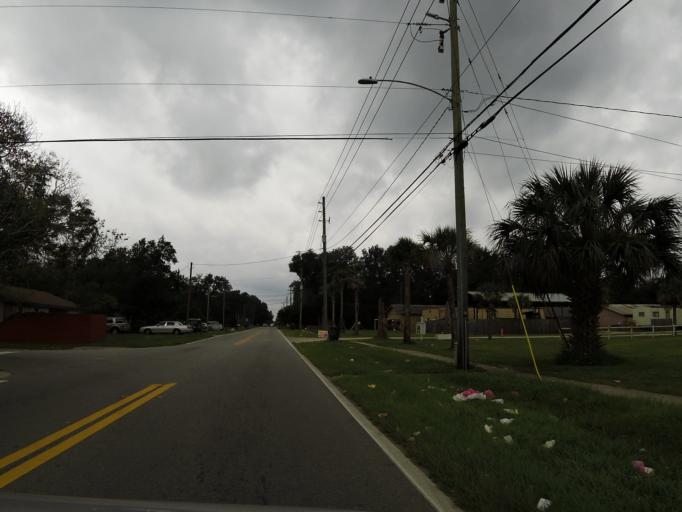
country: US
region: Florida
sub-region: Clay County
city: Bellair-Meadowbrook Terrace
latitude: 30.2443
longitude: -81.7731
